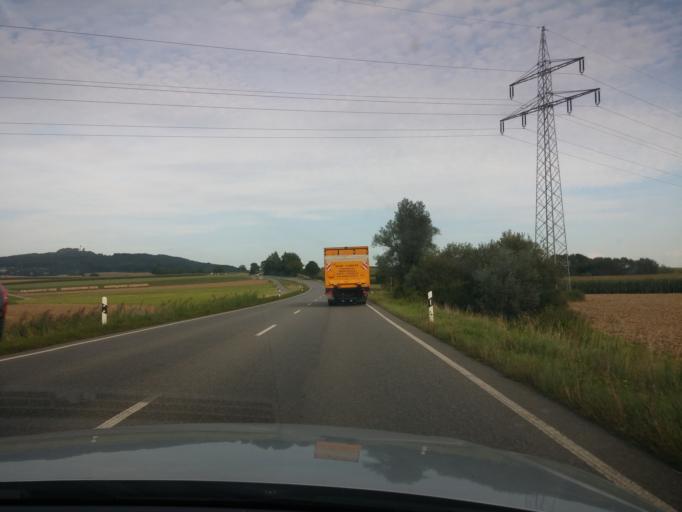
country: DE
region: Baden-Wuerttemberg
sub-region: Tuebingen Region
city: Unlingen
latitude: 48.1529
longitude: 9.5071
